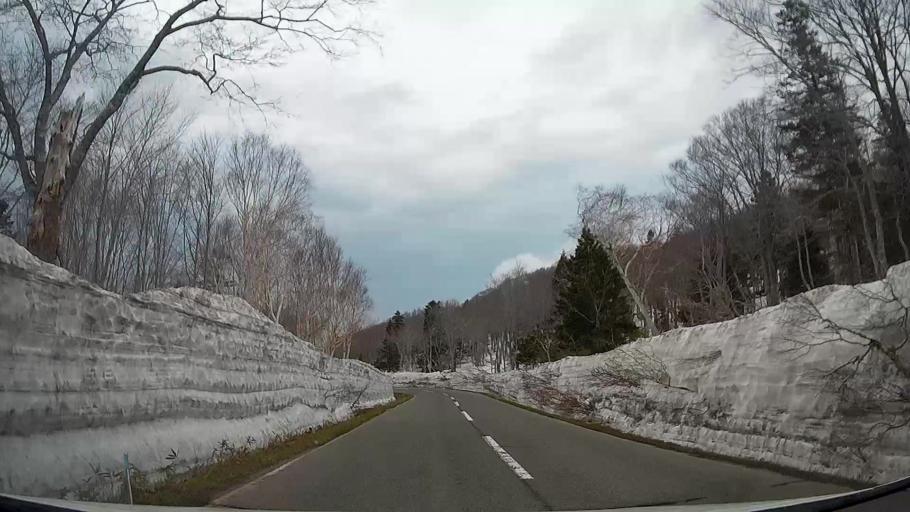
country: JP
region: Aomori
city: Aomori Shi
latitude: 40.6402
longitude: 140.8620
